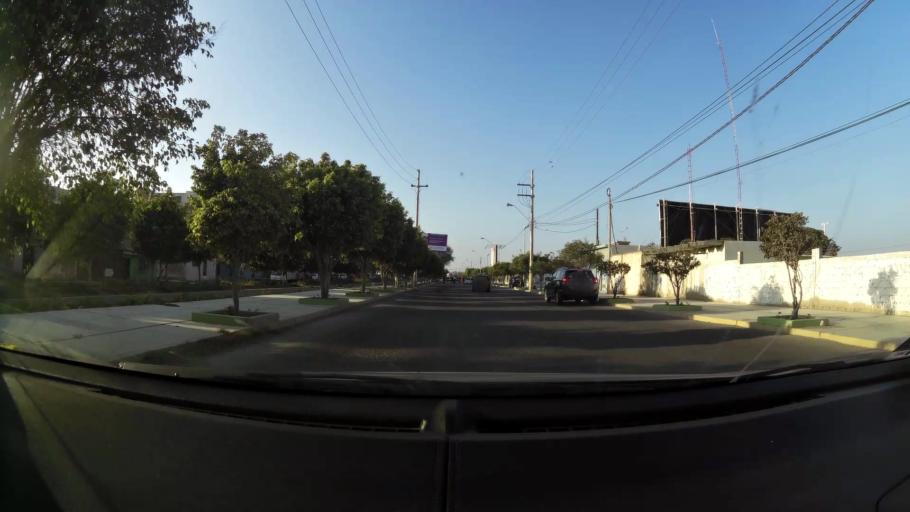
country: PE
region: Lambayeque
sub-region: Provincia de Chiclayo
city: Santa Rosa
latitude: -6.7781
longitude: -79.8300
